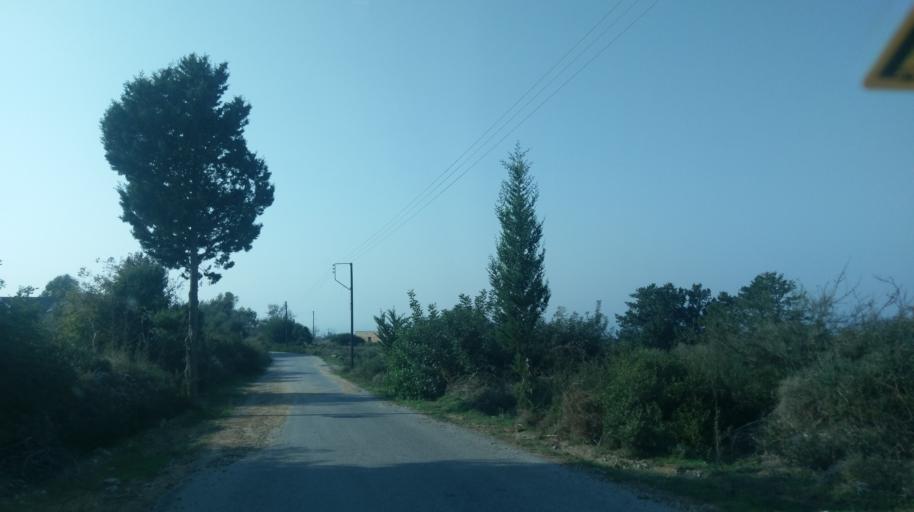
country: CY
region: Ammochostos
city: Leonarisso
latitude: 35.5358
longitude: 34.2302
